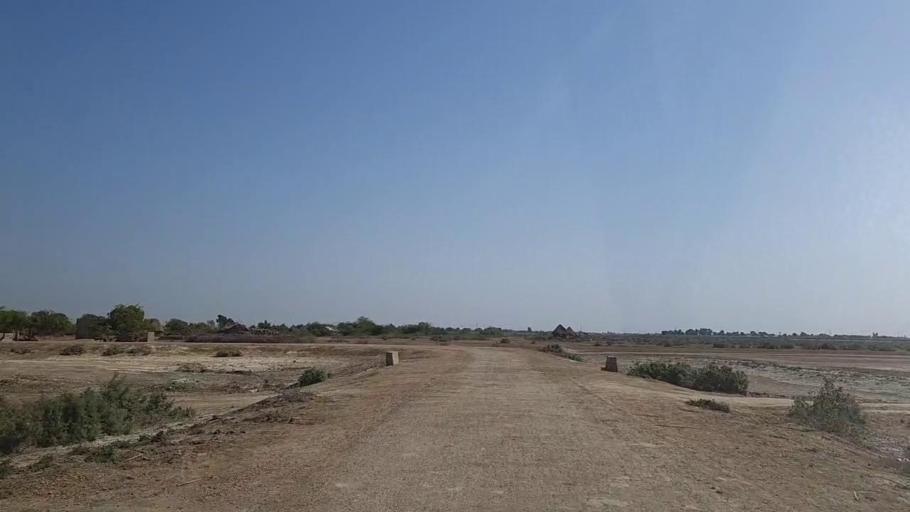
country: PK
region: Sindh
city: Samaro
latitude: 25.2611
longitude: 69.4083
